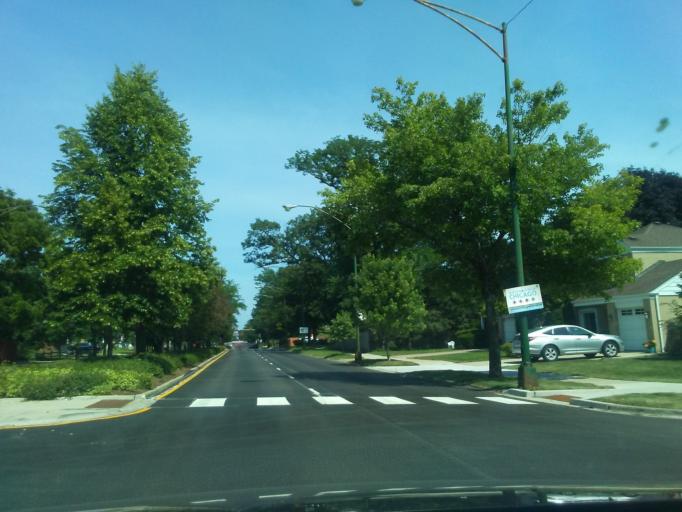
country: US
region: Illinois
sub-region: Cook County
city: Lincolnwood
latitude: 41.9900
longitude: -87.7408
